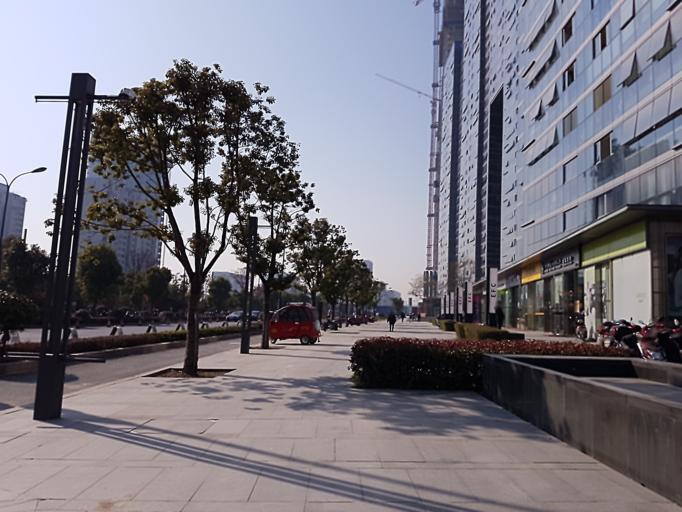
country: CN
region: Zhejiang Sheng
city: Cangqian
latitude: 30.2830
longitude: 120.0017
